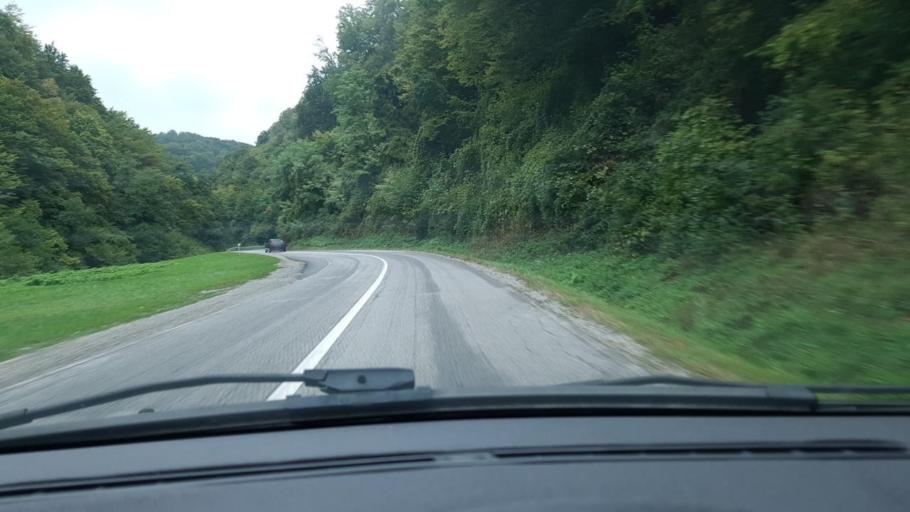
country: HR
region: Krapinsko-Zagorska
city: Marija Bistrica
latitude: 45.9399
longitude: 16.1108
